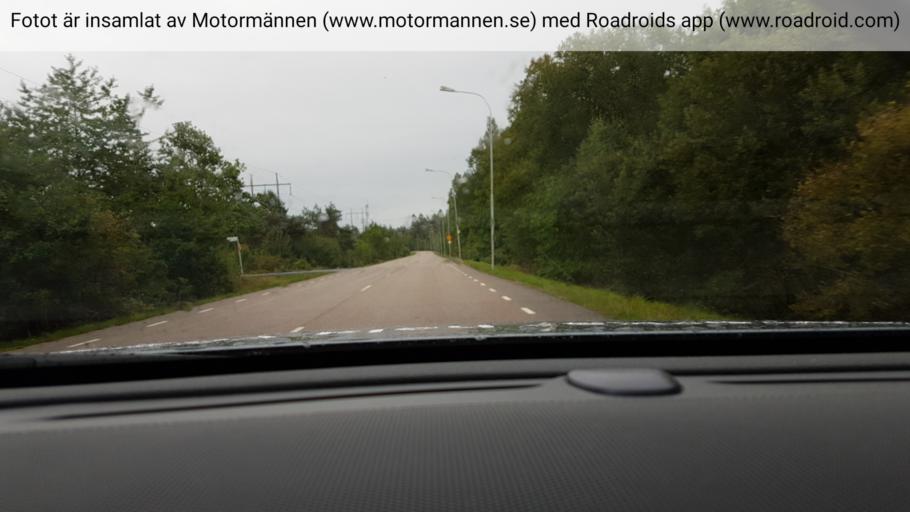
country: SE
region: Vaestra Goetaland
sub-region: Vanersborgs Kommun
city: Vanersborg
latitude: 58.3519
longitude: 12.3446
